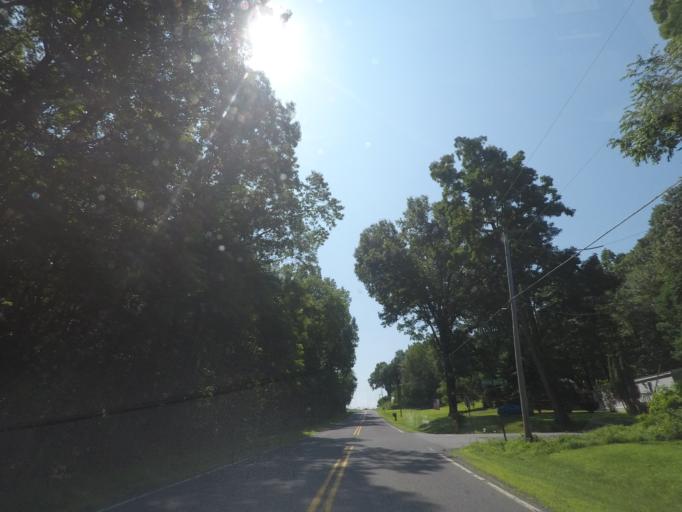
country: US
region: New York
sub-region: Saratoga County
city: Mechanicville
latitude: 42.8546
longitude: -73.7189
